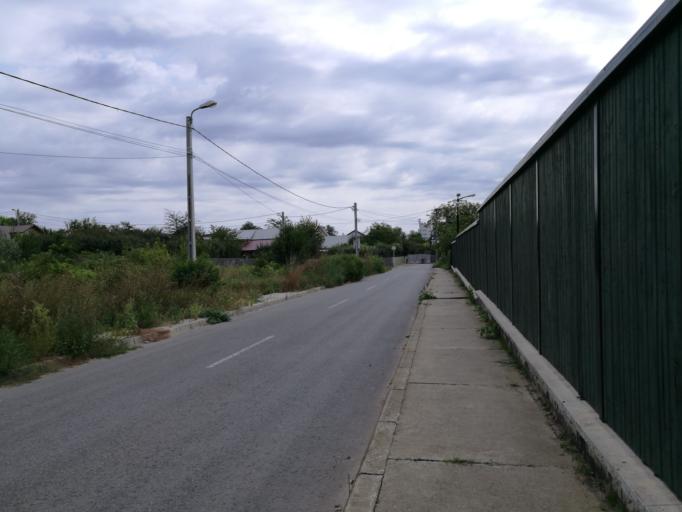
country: RO
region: Iasi
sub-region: Comuna Miroslava
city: Miroslava
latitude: 47.1751
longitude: 27.5270
